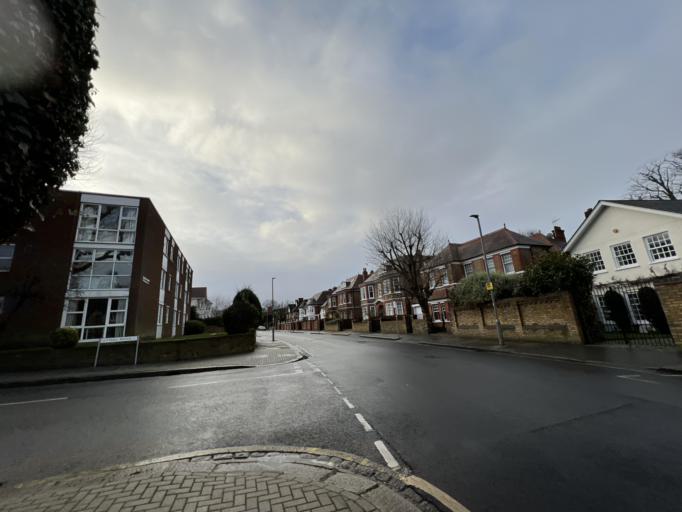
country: GB
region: England
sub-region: Greater London
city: Wandsworth
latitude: 51.4608
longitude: -0.2320
